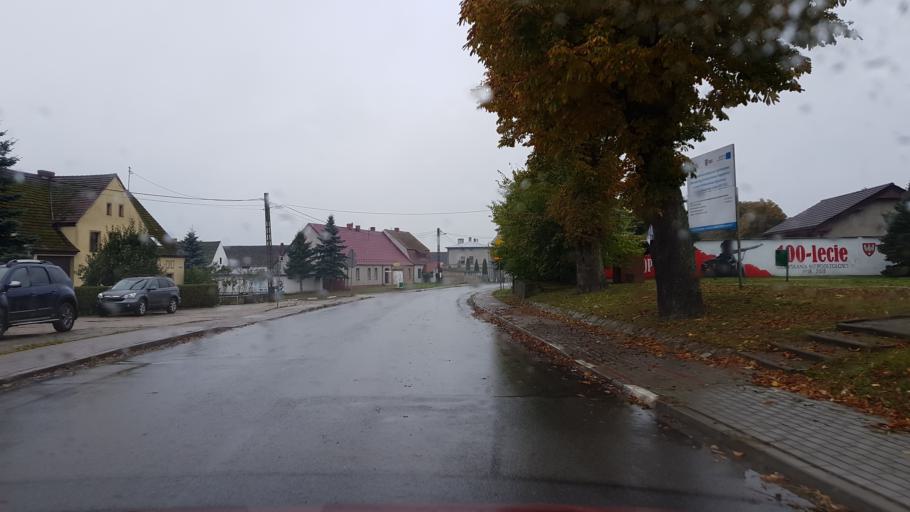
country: PL
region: Greater Poland Voivodeship
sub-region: Powiat zlotowski
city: Tarnowka
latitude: 53.3408
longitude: 16.8523
